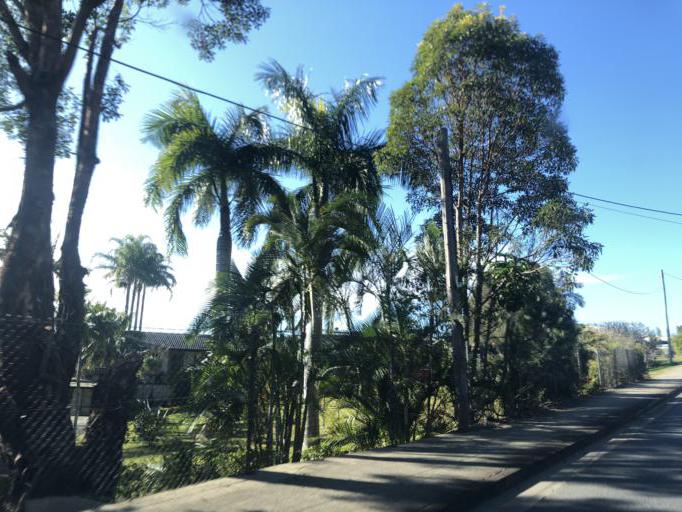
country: AU
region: New South Wales
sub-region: Coffs Harbour
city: Toormina
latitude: -30.3396
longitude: 153.0836
